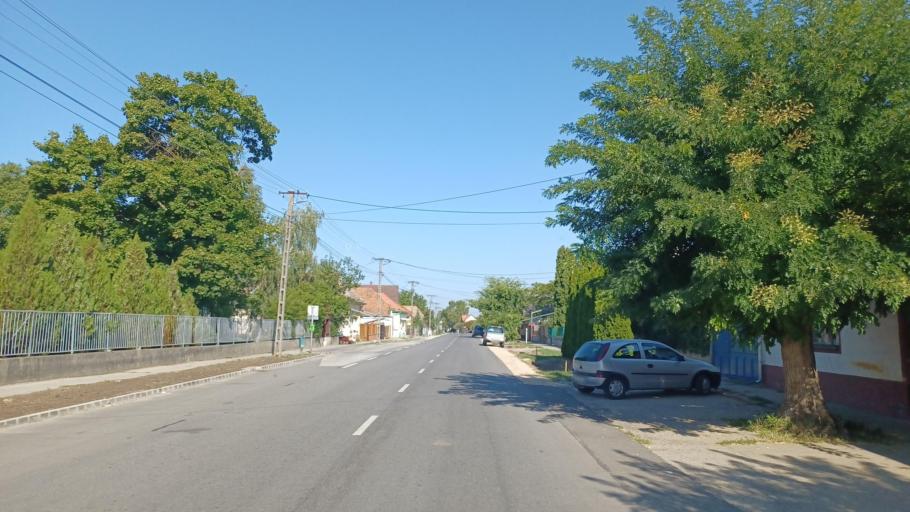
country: HU
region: Tolna
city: Nemetker
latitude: 46.7170
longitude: 18.7643
